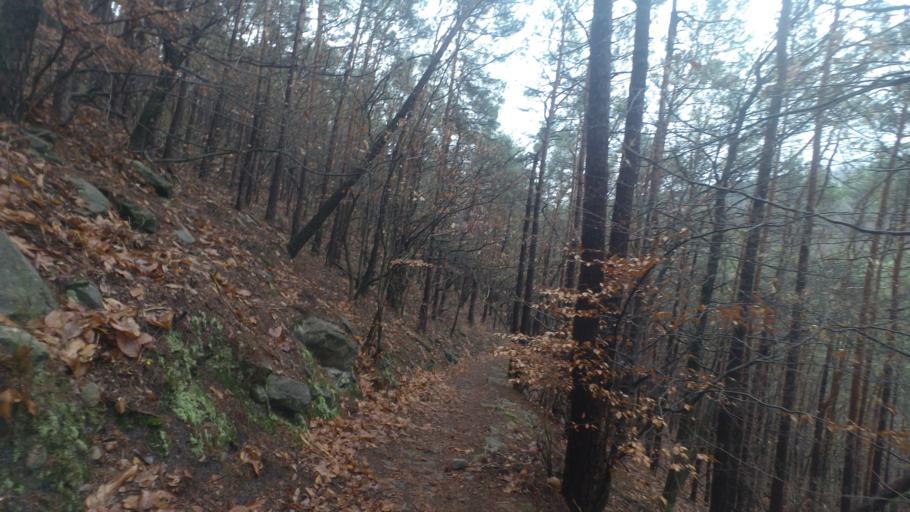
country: DE
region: Rheinland-Pfalz
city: Neustadt
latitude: 49.3808
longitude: 8.1403
